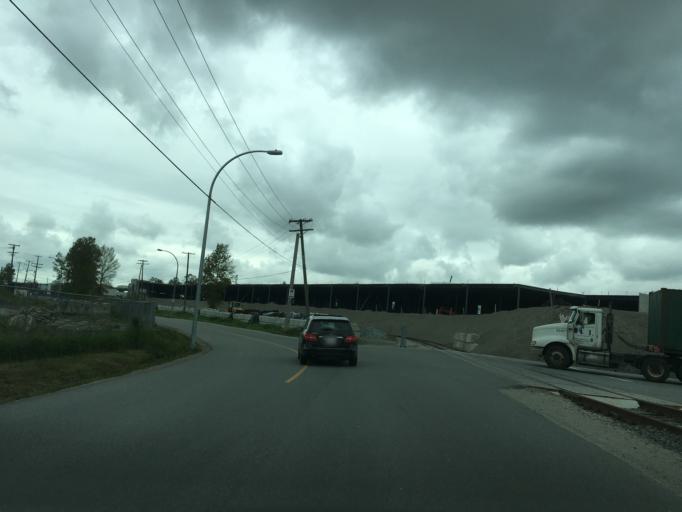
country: CA
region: British Columbia
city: New Westminster
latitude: 49.1953
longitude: -122.9354
